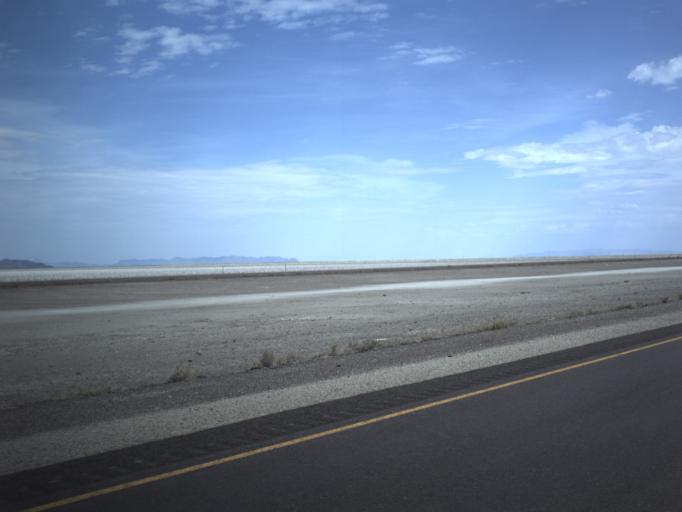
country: US
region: Utah
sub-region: Tooele County
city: Wendover
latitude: 40.7374
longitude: -113.7978
